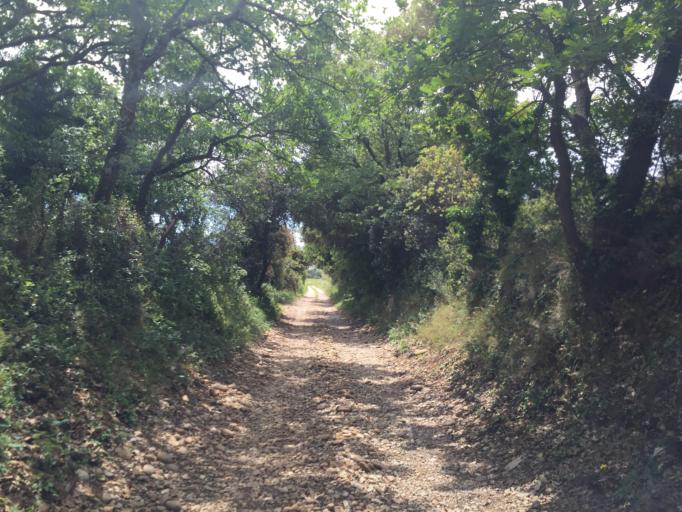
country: FR
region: Provence-Alpes-Cote d'Azur
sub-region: Departement du Vaucluse
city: Bedarrides
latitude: 44.0429
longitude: 4.8717
